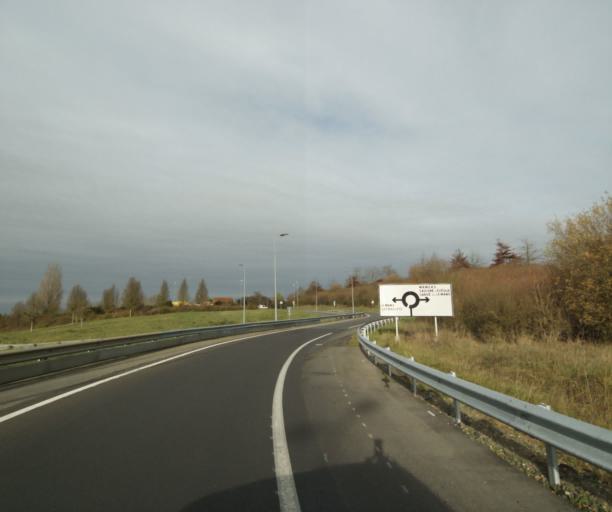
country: FR
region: Pays de la Loire
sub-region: Departement de la Sarthe
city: Sarge-les-le-Mans
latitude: 48.0213
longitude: 0.2319
